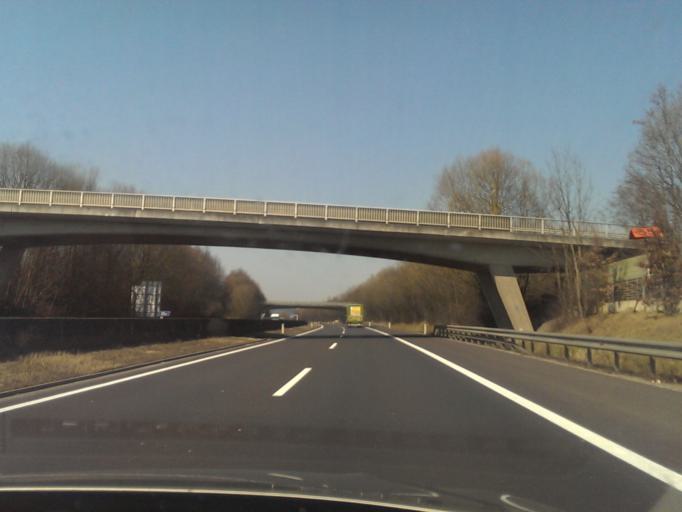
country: AT
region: Upper Austria
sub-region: Politischer Bezirk Ried im Innkreis
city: Ried im Innkreis
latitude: 48.2596
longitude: 13.5106
